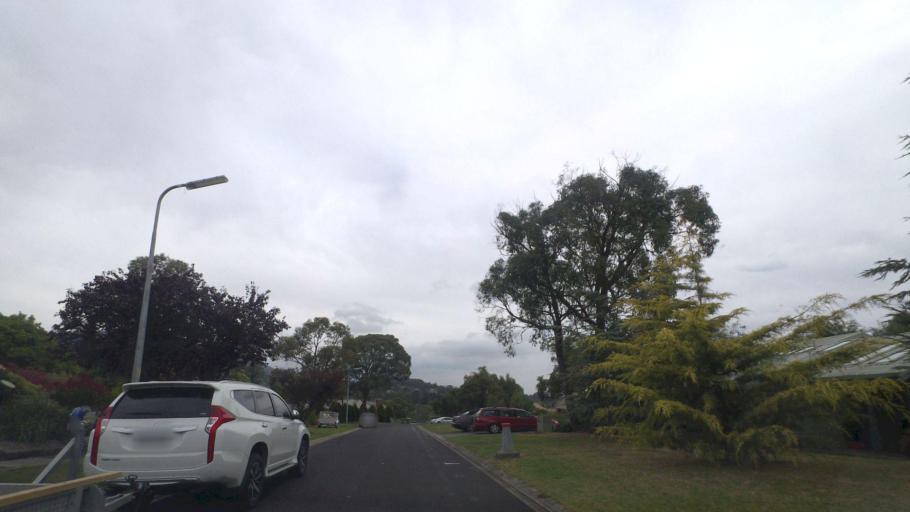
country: AU
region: Victoria
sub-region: Yarra Ranges
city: Kilsyth
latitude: -37.7976
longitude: 145.3357
